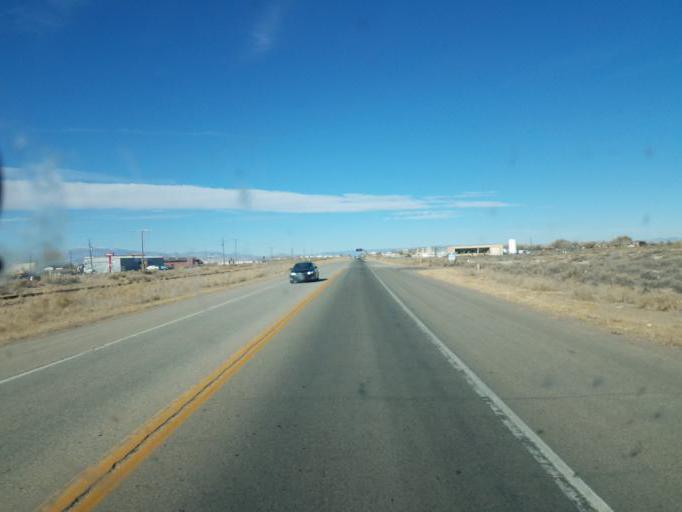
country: US
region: Colorado
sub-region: Alamosa County
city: Alamosa
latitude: 37.4845
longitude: -105.9166
